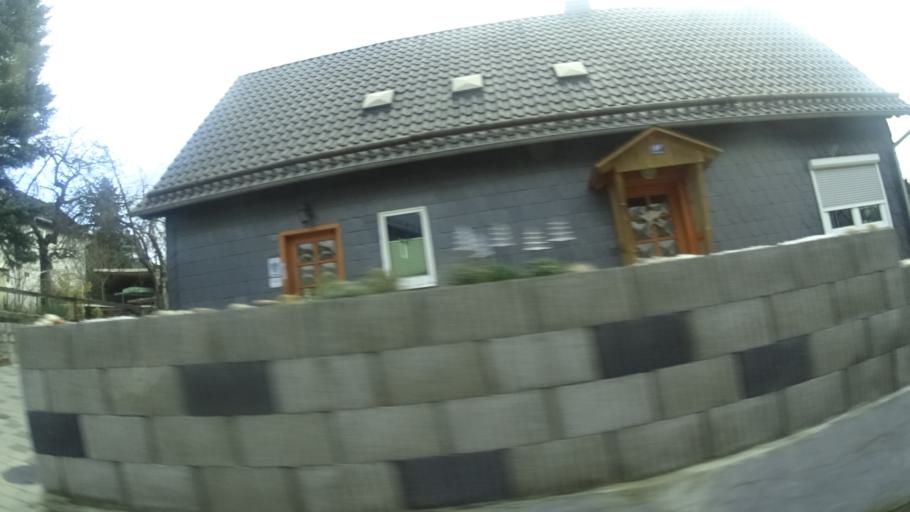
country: DE
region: Thuringia
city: Doschnitz
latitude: 50.6131
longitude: 11.2929
